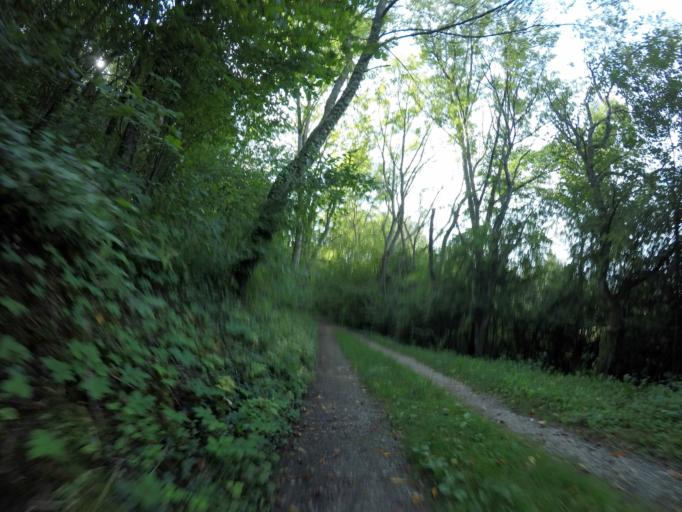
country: DE
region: Baden-Wuerttemberg
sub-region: Tuebingen Region
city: Pfullingen
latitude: 48.4729
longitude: 9.2120
